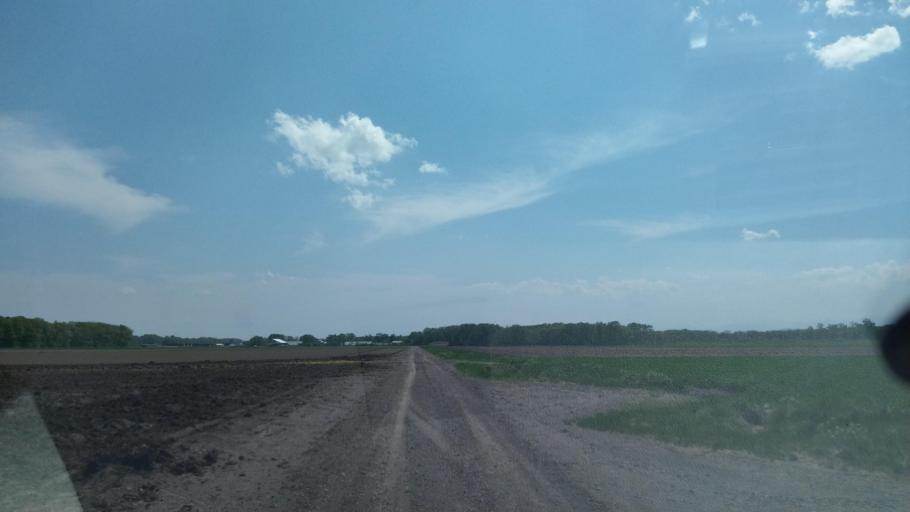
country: JP
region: Hokkaido
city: Otofuke
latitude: 43.1409
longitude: 143.2208
